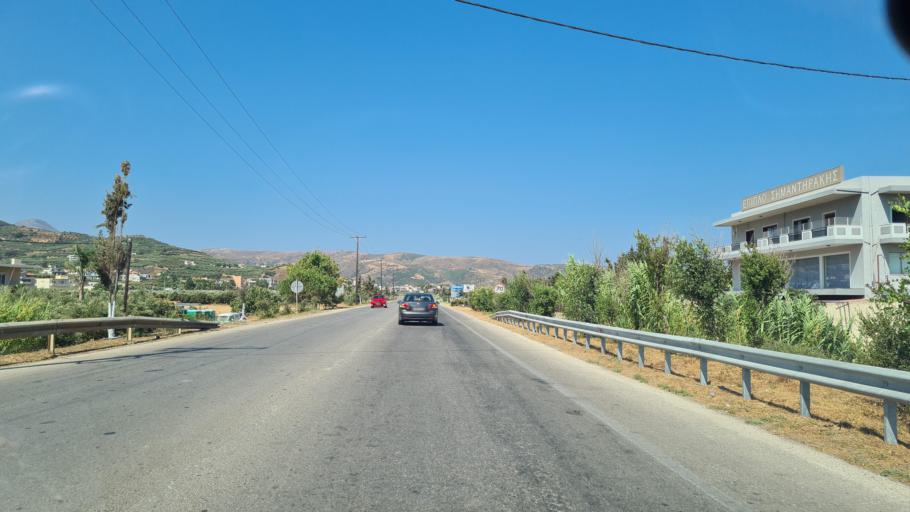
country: GR
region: Crete
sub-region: Nomos Chanias
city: Kissamos
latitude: 35.4942
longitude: 23.6743
